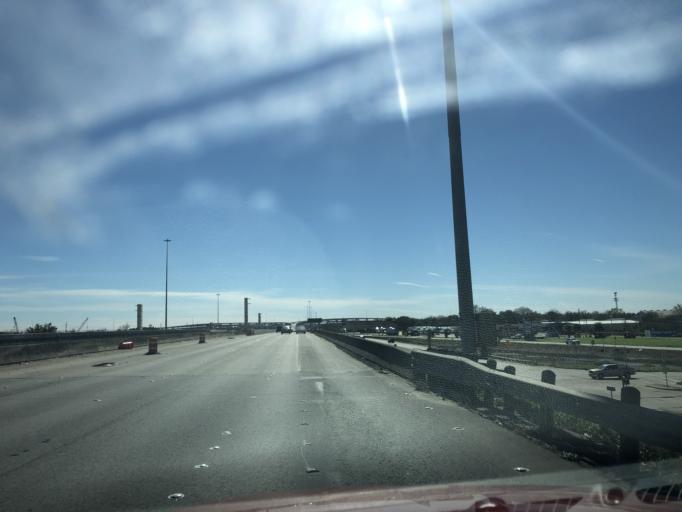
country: US
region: Texas
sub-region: Brazoria County
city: Brookside Village
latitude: 29.6147
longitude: -95.3873
